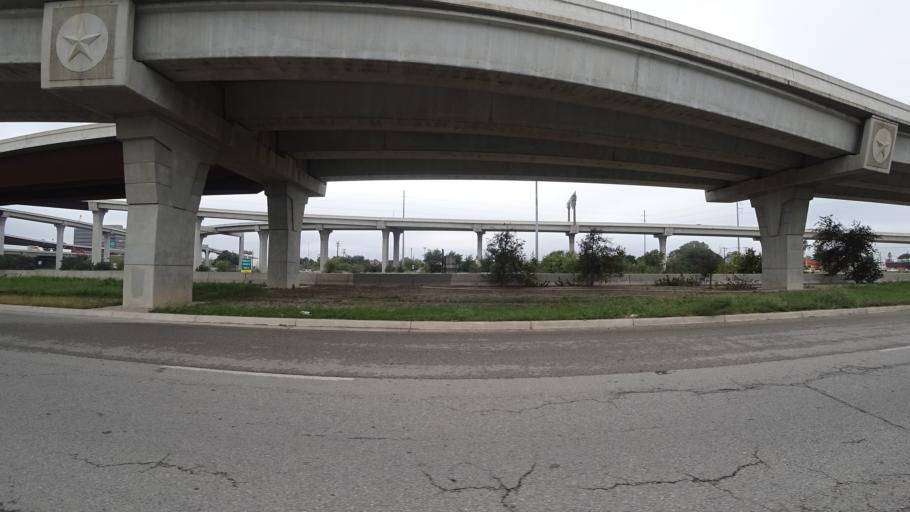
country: US
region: Texas
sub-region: Travis County
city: Austin
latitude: 30.2176
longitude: -97.7531
